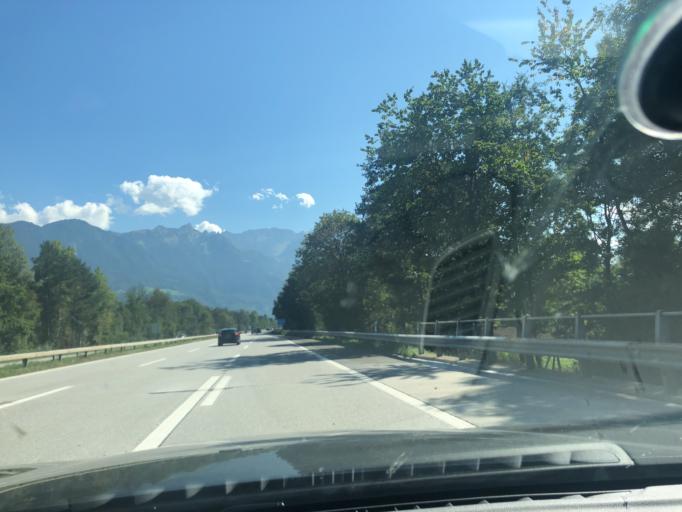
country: LI
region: Vaduz
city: Vaduz
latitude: 47.1446
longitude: 9.5017
